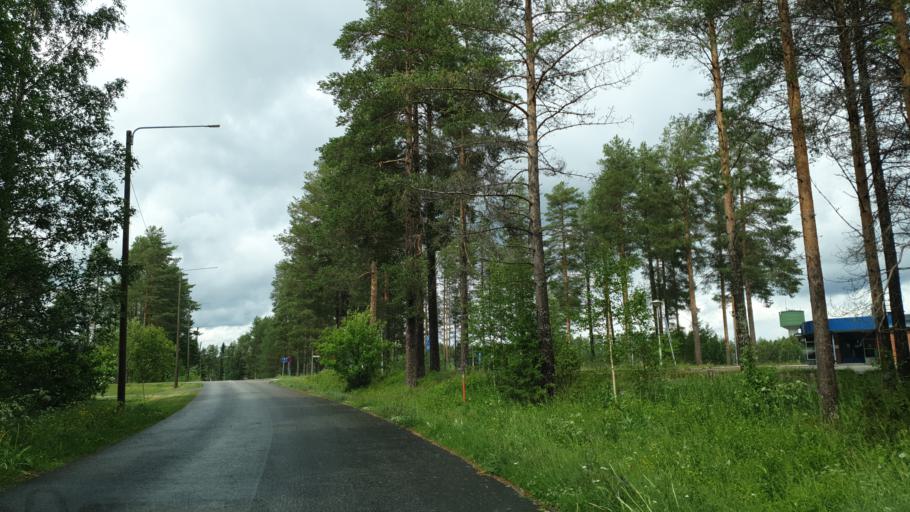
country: FI
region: Kainuu
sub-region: Kehys-Kainuu
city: Kuhmo
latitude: 64.1168
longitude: 29.5172
